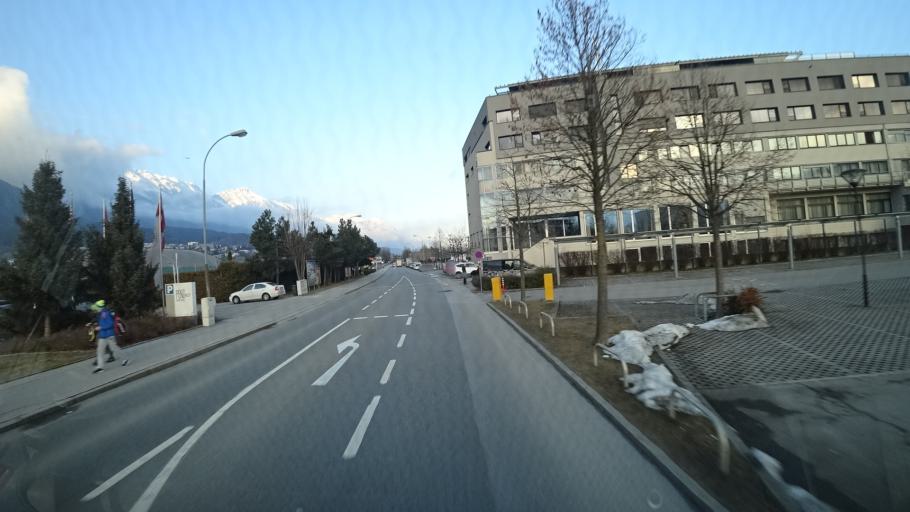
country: AT
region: Tyrol
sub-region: Politischer Bezirk Innsbruck Land
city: Vols
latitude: 47.2577
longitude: 11.3571
